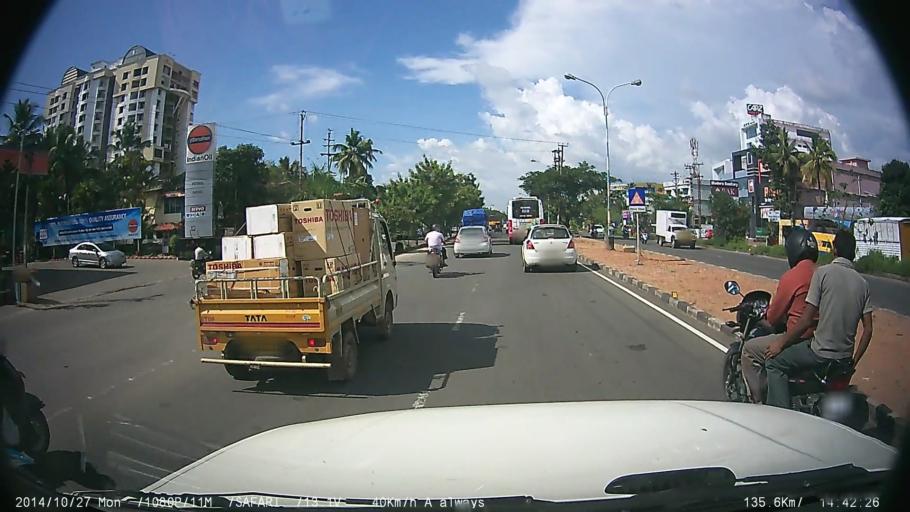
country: IN
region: Kerala
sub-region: Ernakulam
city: Elur
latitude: 10.0105
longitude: 76.3121
